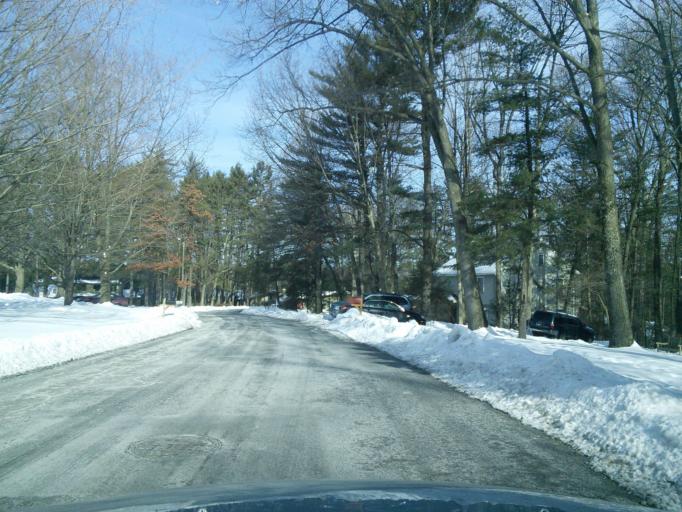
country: US
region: Pennsylvania
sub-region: Centre County
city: State College
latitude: 40.8290
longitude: -77.8816
